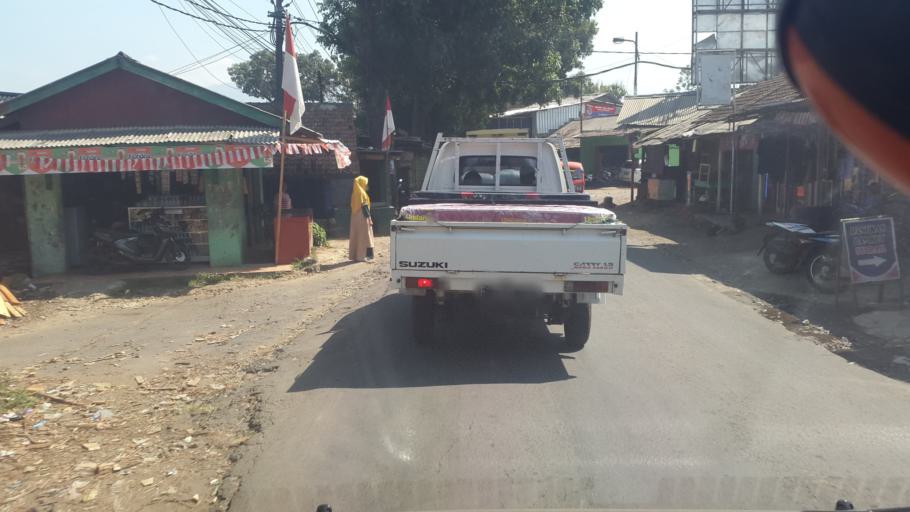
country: ID
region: West Java
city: Cicurug
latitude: -6.8300
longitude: 106.7387
